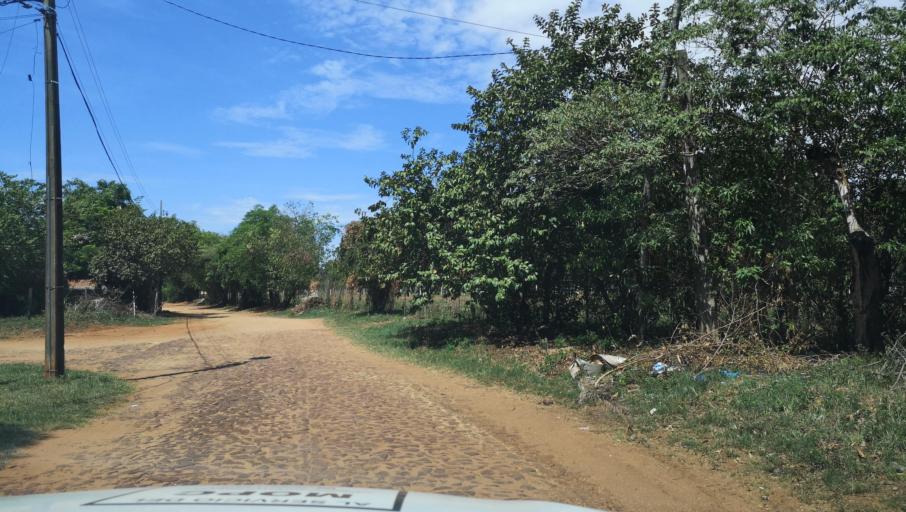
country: PY
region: Misiones
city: Santa Maria
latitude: -26.8984
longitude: -57.0291
